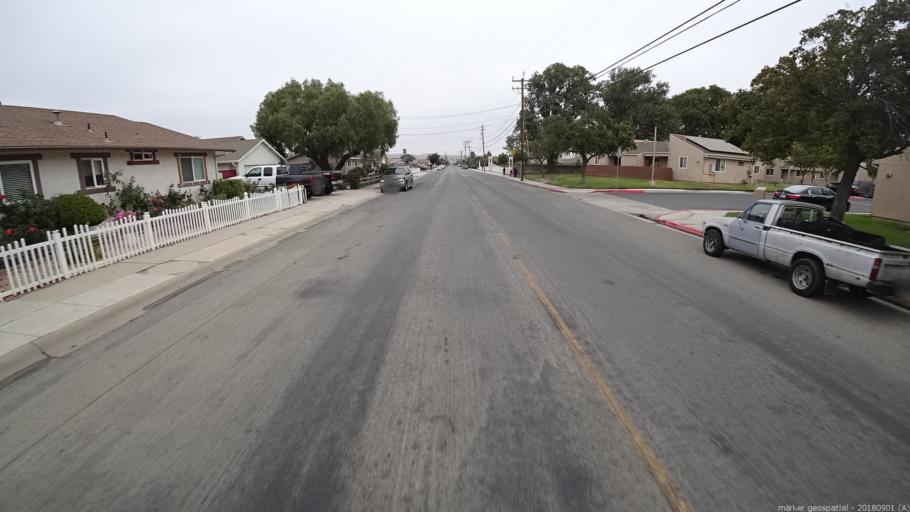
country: US
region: California
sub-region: Monterey County
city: Greenfield
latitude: 36.3163
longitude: -121.2436
